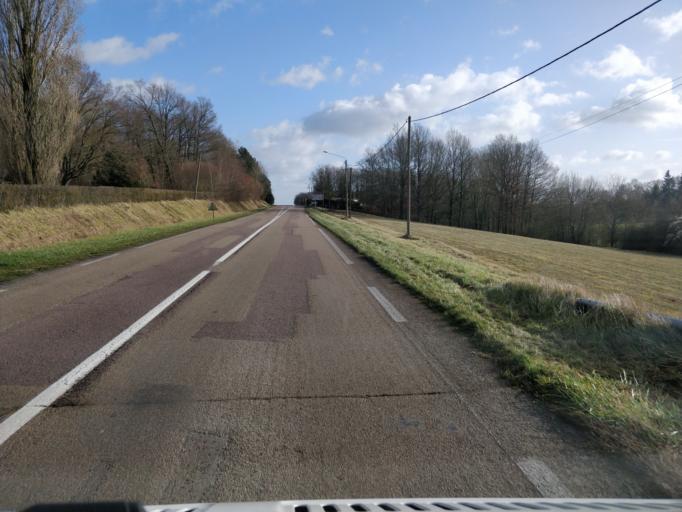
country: FR
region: Bourgogne
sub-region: Departement de l'Yonne
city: Cheroy
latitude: 48.2003
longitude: 3.0119
